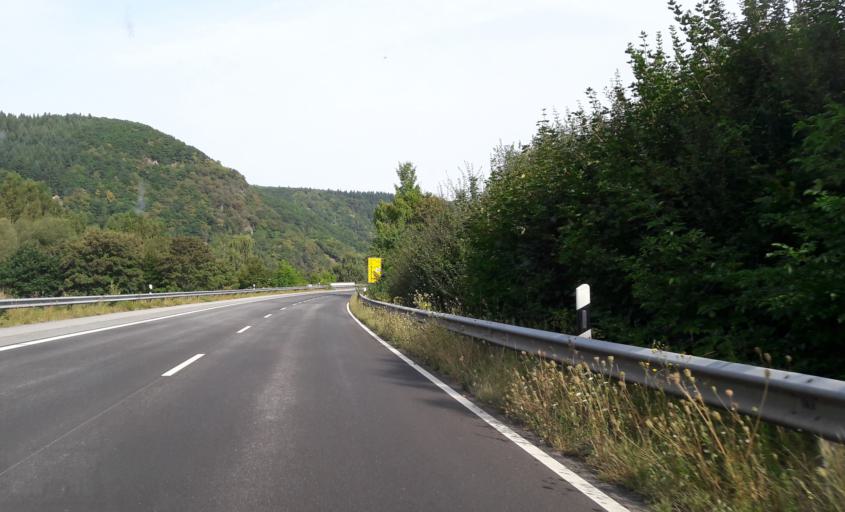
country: DE
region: Rheinland-Pfalz
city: Enkirch
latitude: 49.9868
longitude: 7.1199
